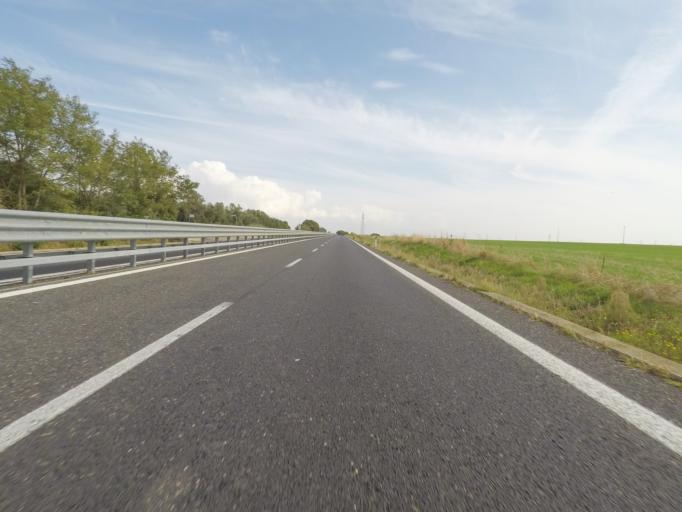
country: IT
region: Latium
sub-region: Provincia di Viterbo
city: Pescia Romana
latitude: 42.3925
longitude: 11.5339
